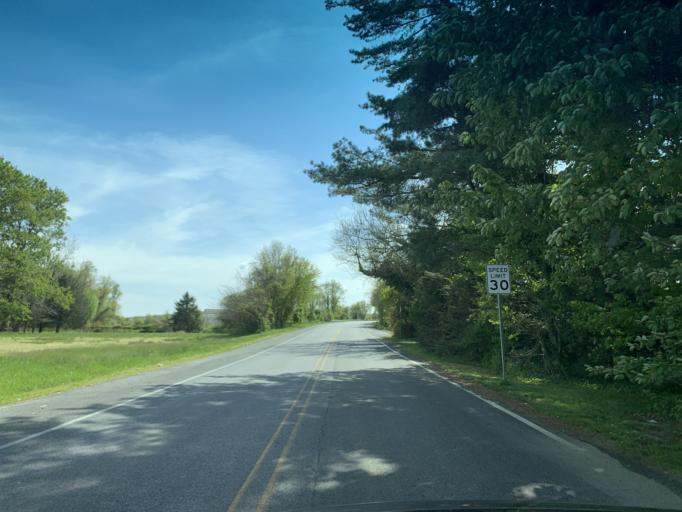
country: US
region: Maryland
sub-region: Harford County
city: Perryman
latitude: 39.4641
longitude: -76.1990
